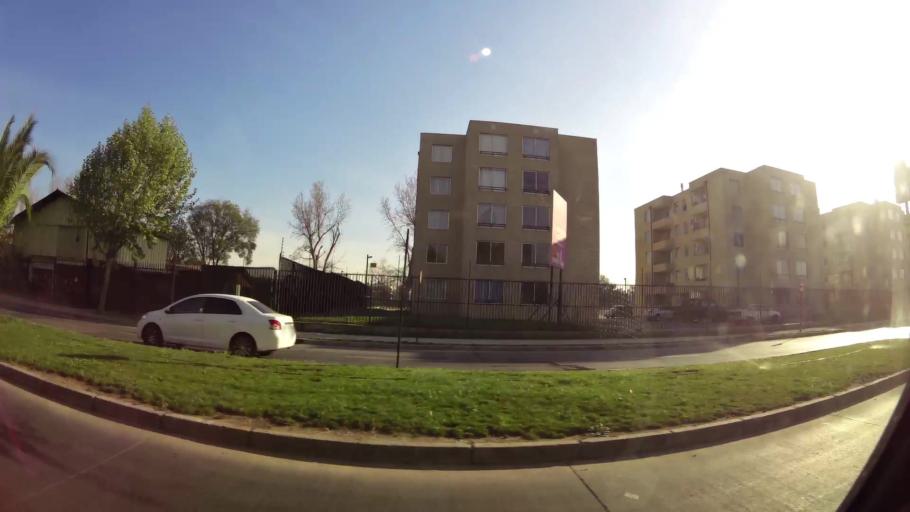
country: CL
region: Santiago Metropolitan
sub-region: Provincia de Santiago
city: Lo Prado
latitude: -33.4529
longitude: -70.7463
